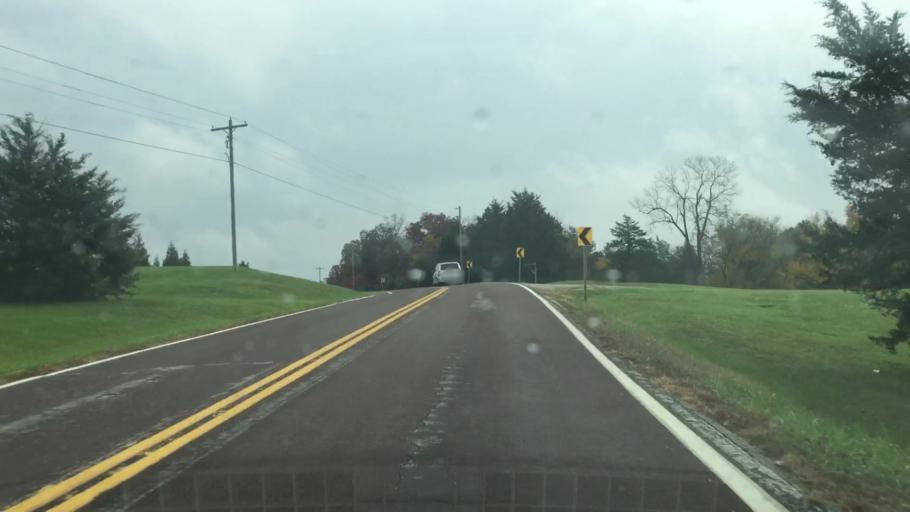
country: US
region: Missouri
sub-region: Callaway County
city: Fulton
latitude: 38.7787
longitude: -91.8448
